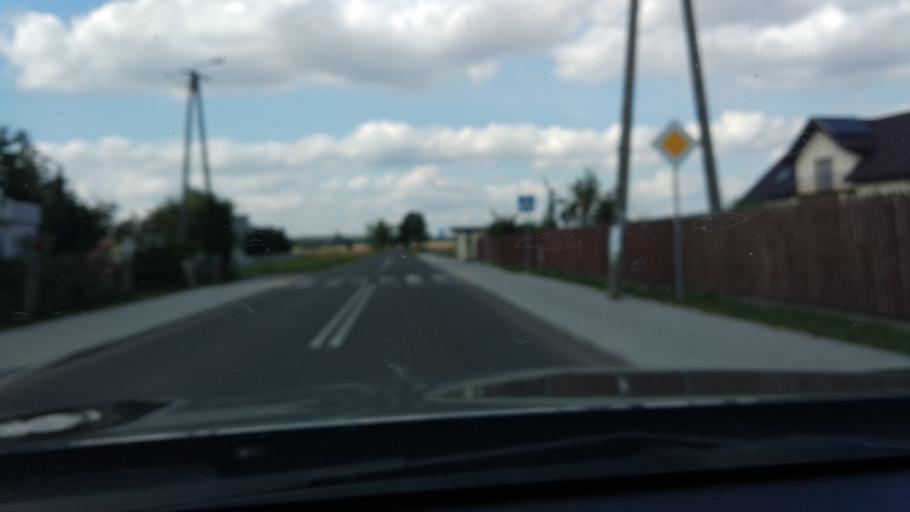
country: PL
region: Masovian Voivodeship
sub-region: Powiat pultuski
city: Zatory
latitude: 52.5613
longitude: 21.1870
